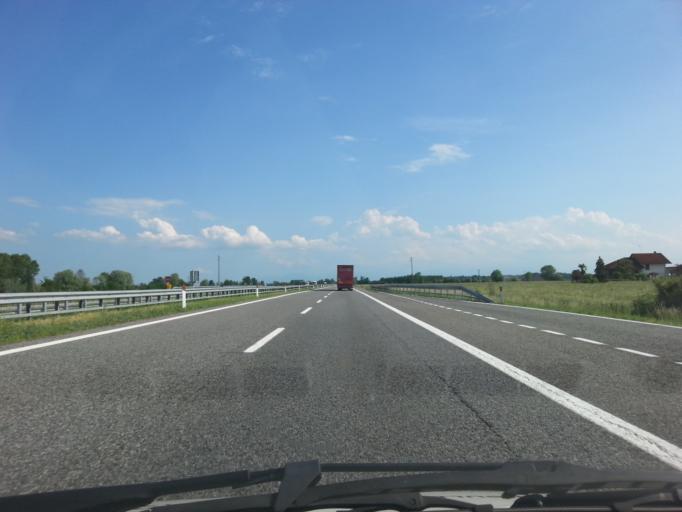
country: IT
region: Piedmont
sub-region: Provincia di Cuneo
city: Marene
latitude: 44.6906
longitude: 7.7670
